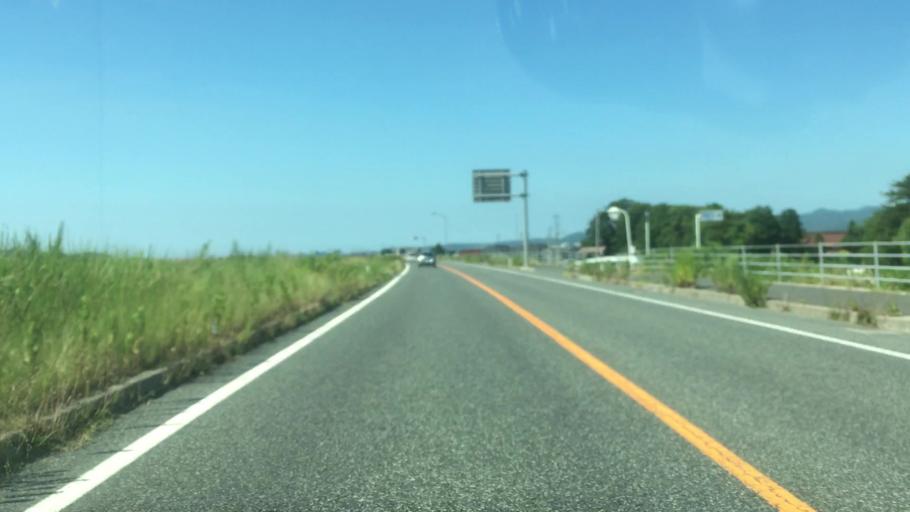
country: JP
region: Tottori
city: Tottori
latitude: 35.4544
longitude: 134.2151
